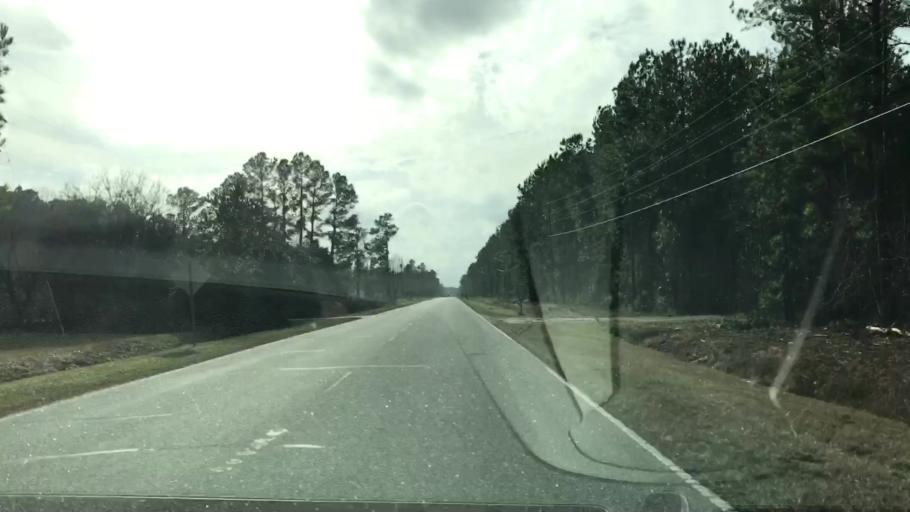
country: US
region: South Carolina
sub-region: Williamsburg County
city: Andrews
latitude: 33.3702
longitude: -79.6376
